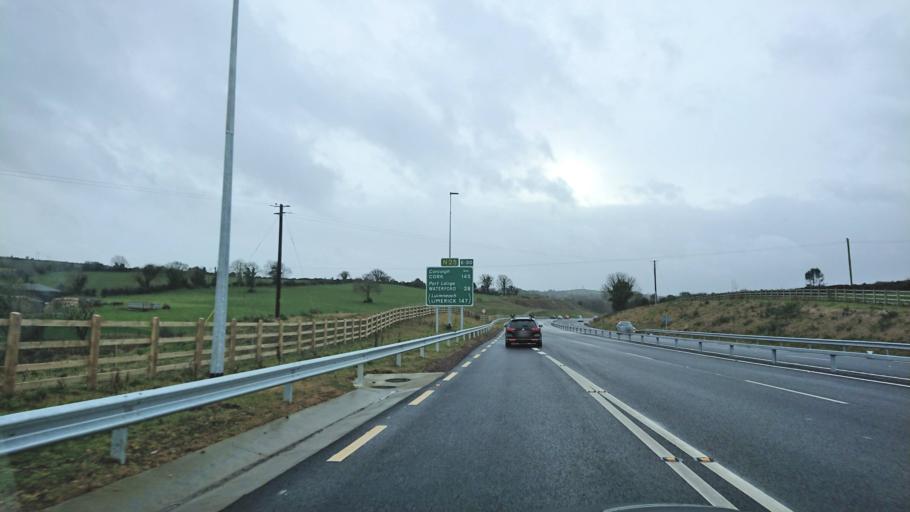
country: IE
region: Leinster
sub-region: Loch Garman
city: New Ross
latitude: 52.3845
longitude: -6.9031
